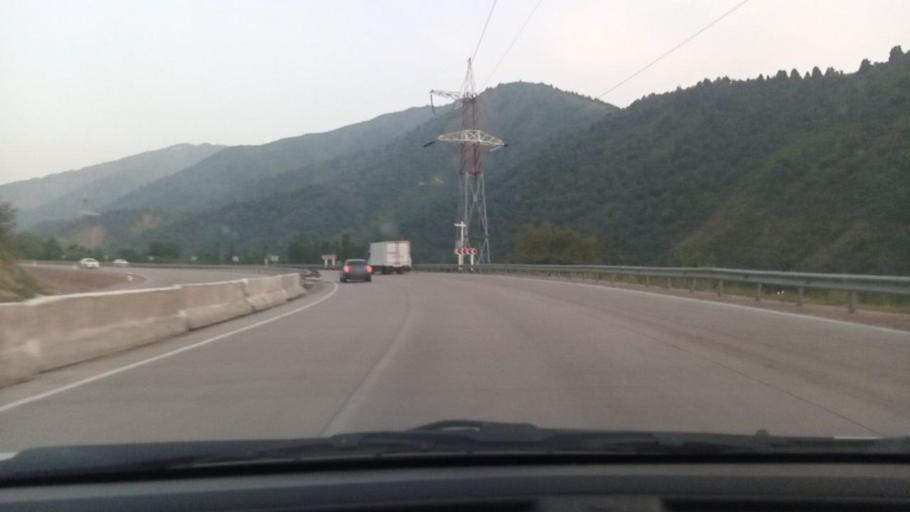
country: UZ
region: Toshkent
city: Angren
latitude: 41.1464
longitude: 70.4461
